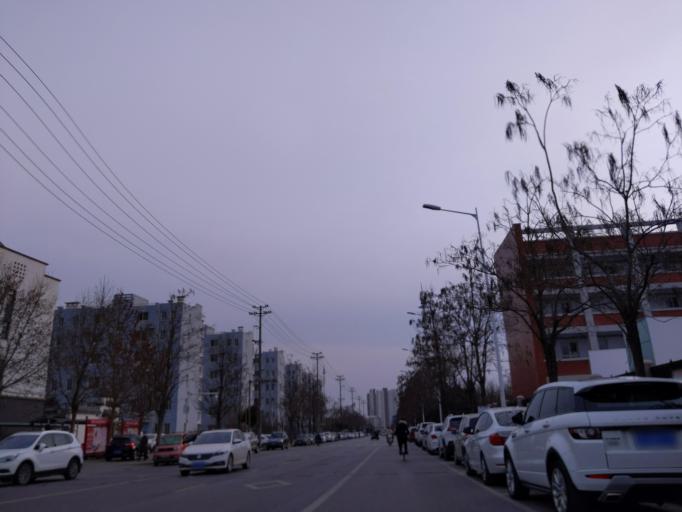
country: CN
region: Henan Sheng
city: Zhongyuanlu
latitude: 35.7599
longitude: 115.0409
